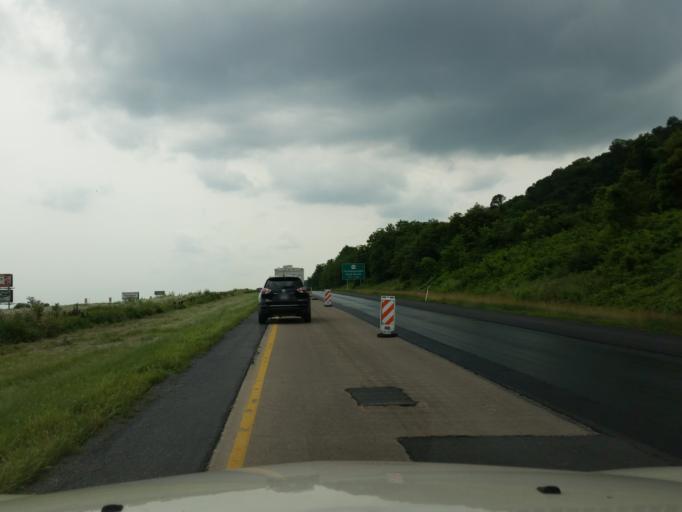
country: US
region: Pennsylvania
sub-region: Perry County
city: Newport
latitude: 40.5711
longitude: -77.2142
